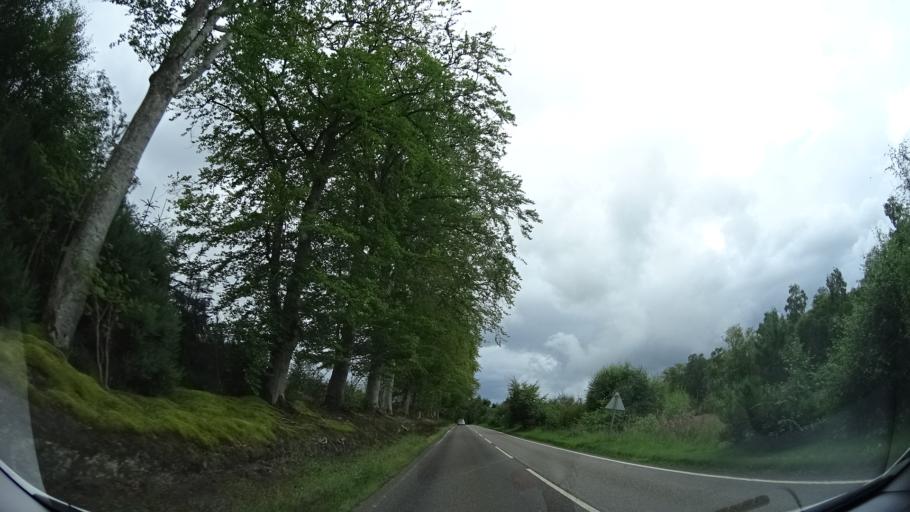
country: GB
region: Scotland
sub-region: Highland
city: Inverness
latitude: 57.5388
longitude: -4.2627
